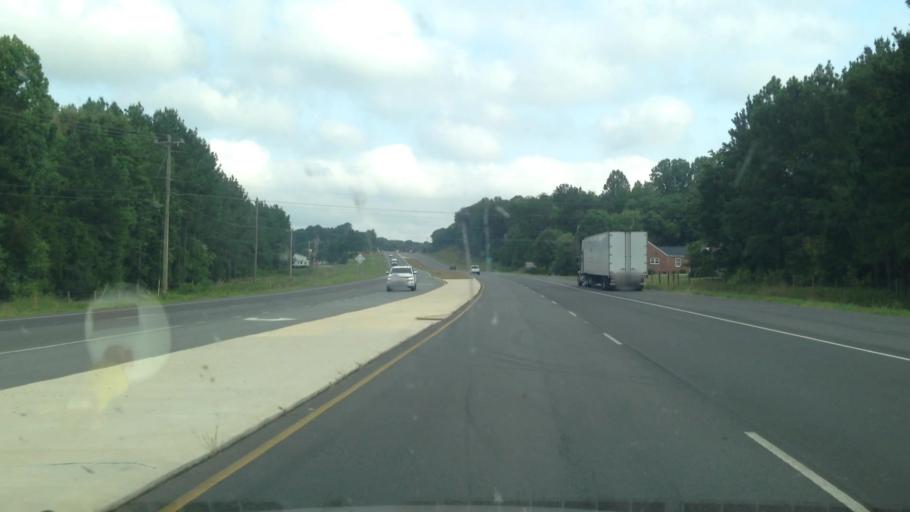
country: US
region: North Carolina
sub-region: Guilford County
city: Summerfield
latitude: 36.1761
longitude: -79.8823
